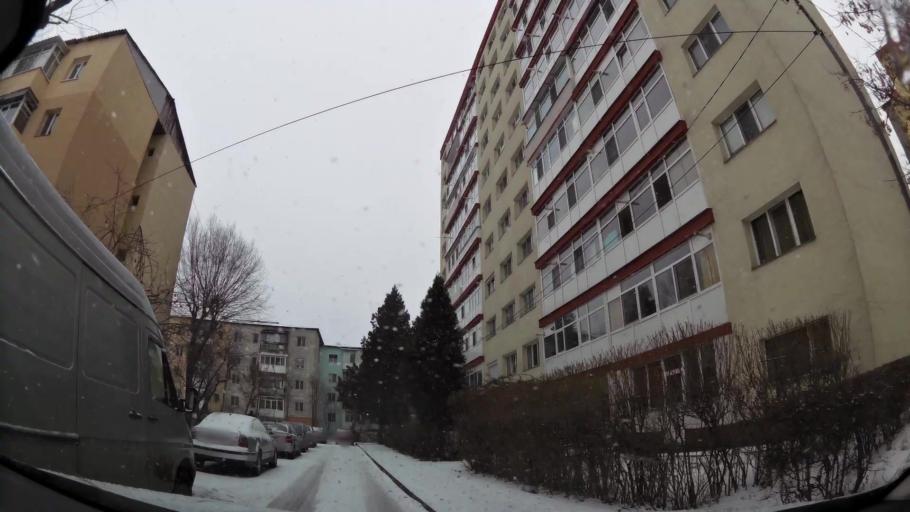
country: RO
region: Dambovita
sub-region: Municipiul Targoviste
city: Targoviste
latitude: 44.9244
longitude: 25.4422
